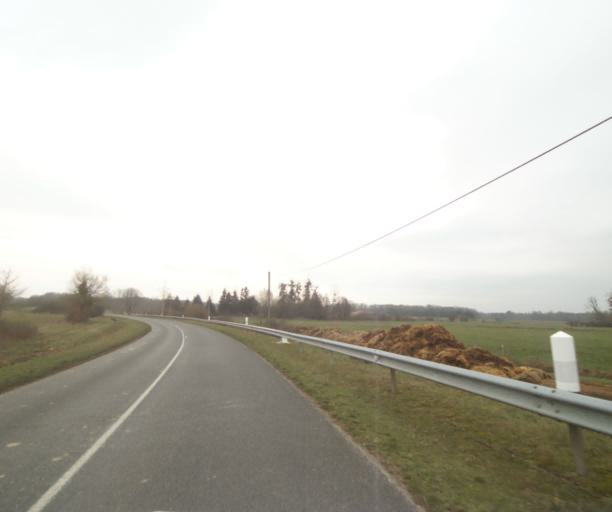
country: FR
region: Champagne-Ardenne
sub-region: Departement de la Marne
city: Pargny-sur-Saulx
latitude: 48.7438
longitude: 4.8487
